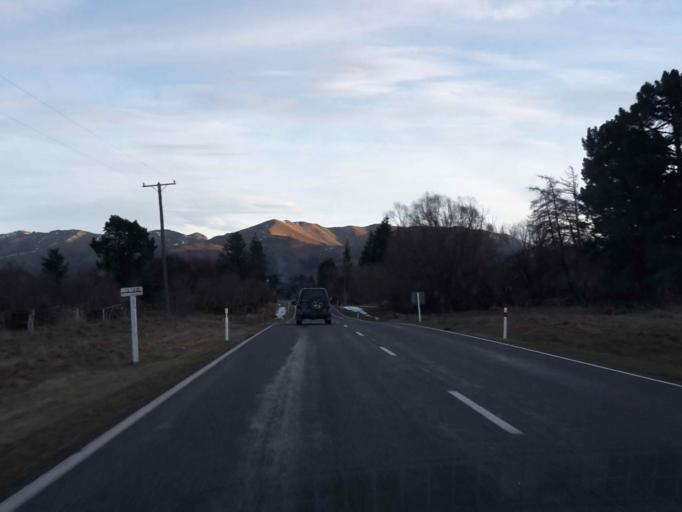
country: NZ
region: Canterbury
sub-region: Timaru District
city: Pleasant Point
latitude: -44.0822
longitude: 170.6611
